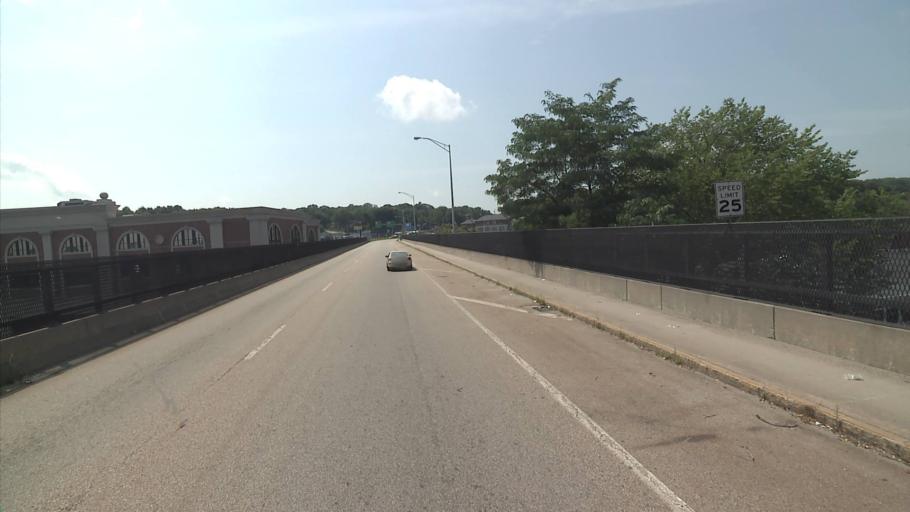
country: US
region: Connecticut
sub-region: New London County
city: Norwich
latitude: 41.5252
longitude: -72.0819
